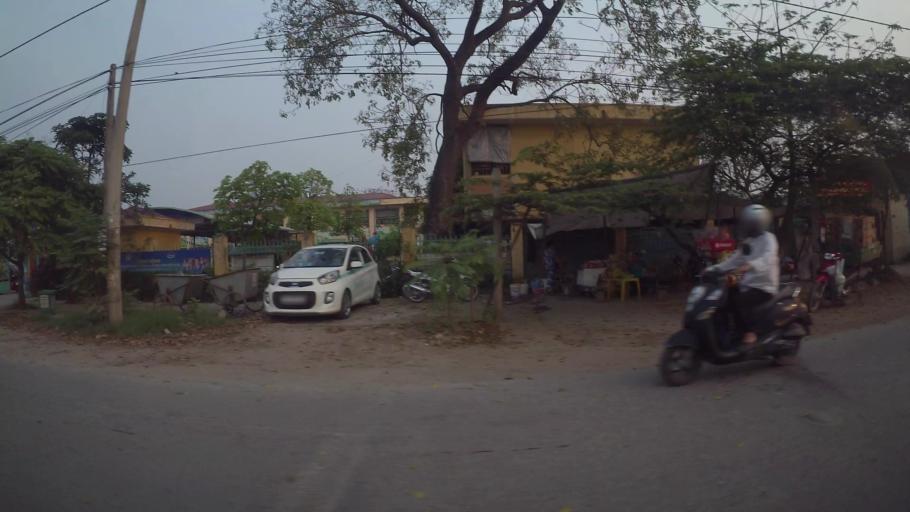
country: VN
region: Ha Noi
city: Kim Bai
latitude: 20.8678
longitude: 105.8102
